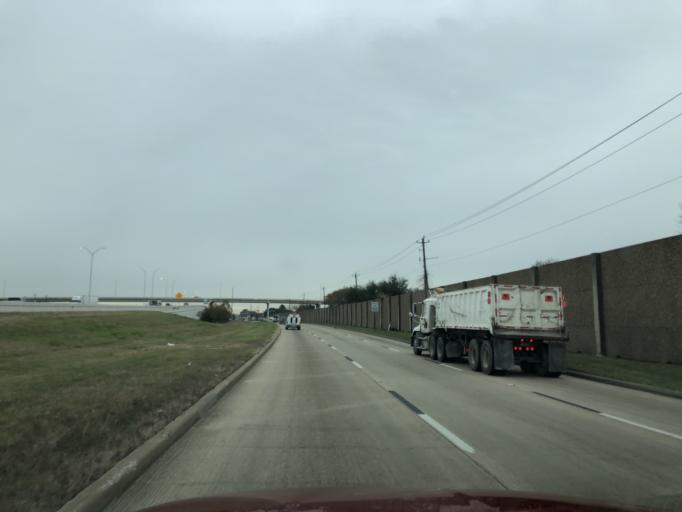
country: US
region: Texas
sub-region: Fort Bend County
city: Missouri City
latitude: 29.6152
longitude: -95.4981
